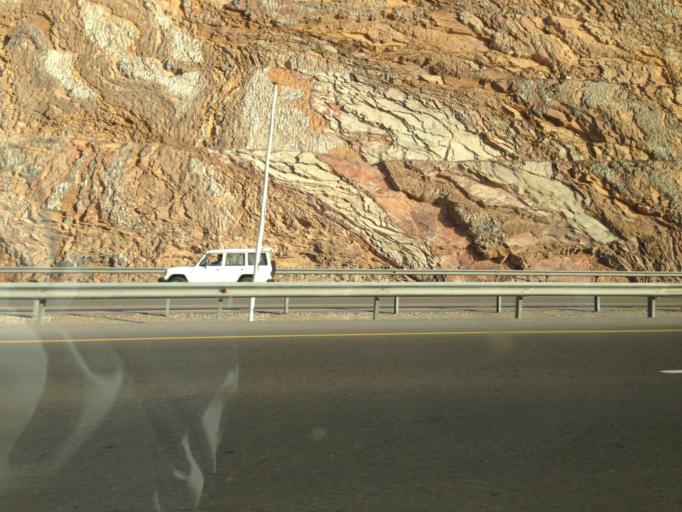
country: OM
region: Muhafazat Masqat
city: Bawshar
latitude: 23.5864
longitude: 58.4566
